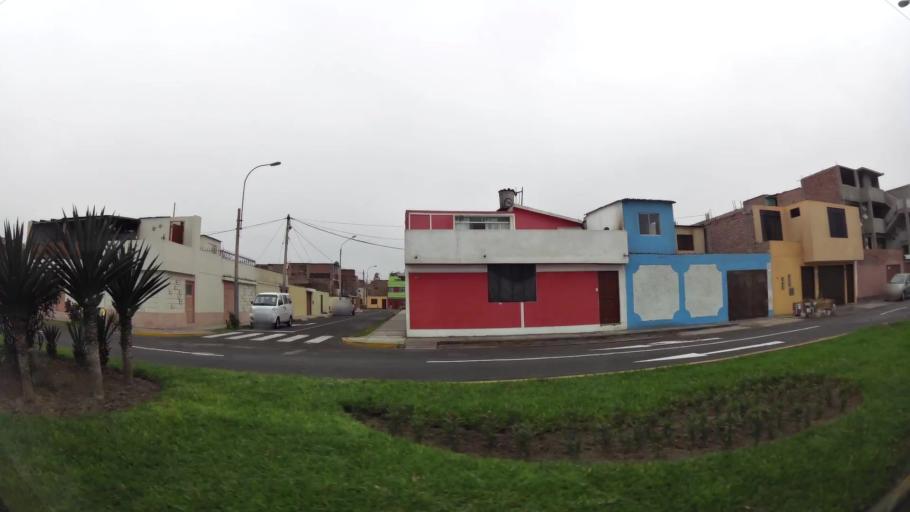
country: PE
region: Callao
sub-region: Callao
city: Callao
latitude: -12.0789
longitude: -77.1103
